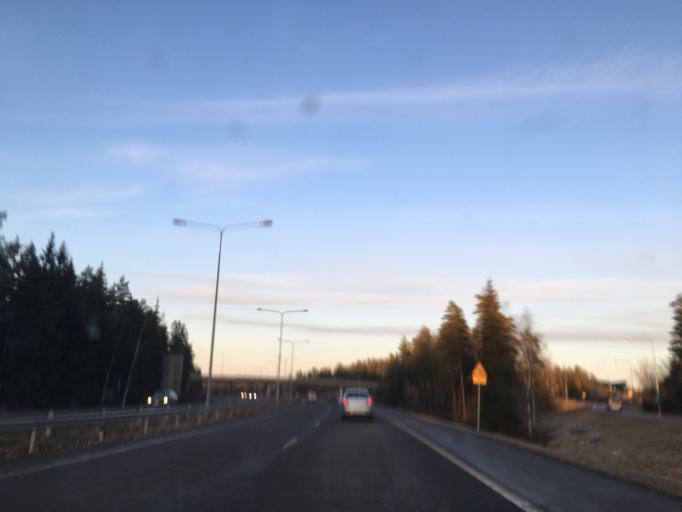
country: FI
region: Varsinais-Suomi
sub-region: Turku
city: Turku
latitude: 60.5054
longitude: 22.2969
